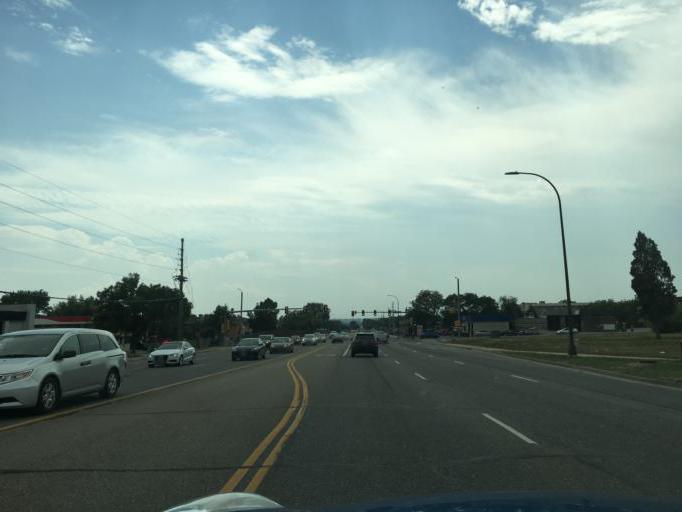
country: US
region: Colorado
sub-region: Jefferson County
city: Arvada
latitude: 39.8215
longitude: -105.0814
